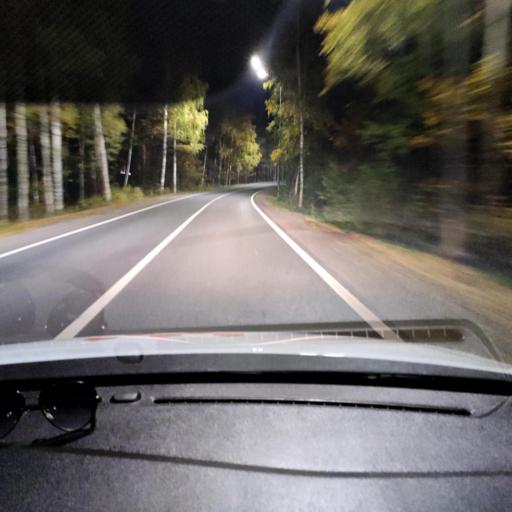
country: RU
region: Tatarstan
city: Verkhniy Uslon
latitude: 55.6336
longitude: 49.0186
